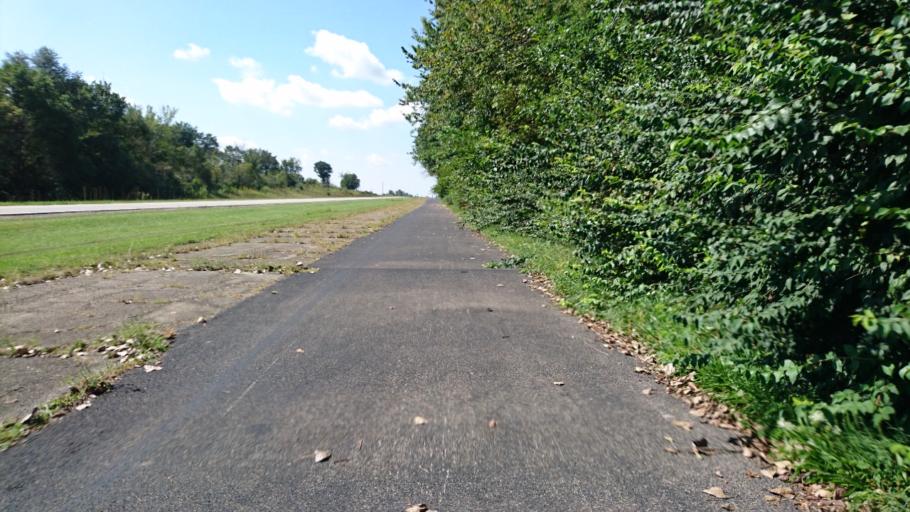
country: US
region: Illinois
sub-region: McLean County
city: Lexington
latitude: 40.6306
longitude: -88.8020
